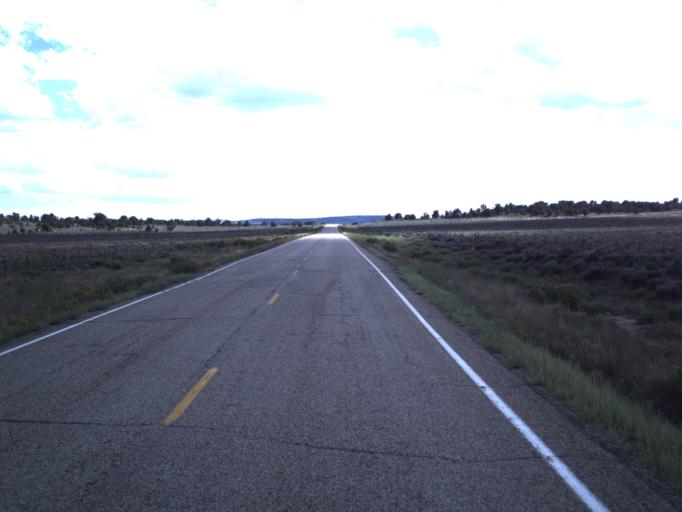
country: US
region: Utah
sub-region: Duchesne County
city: Duchesne
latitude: 40.2531
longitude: -110.7105
